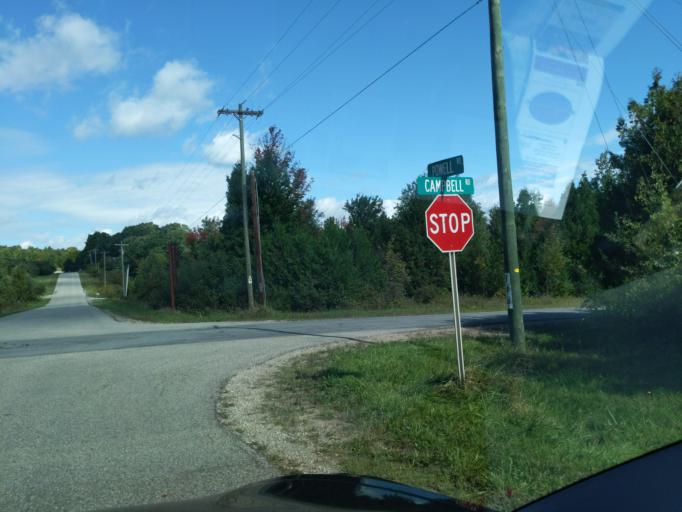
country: US
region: Michigan
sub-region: Antrim County
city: Elk Rapids
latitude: 44.9607
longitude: -85.3323
